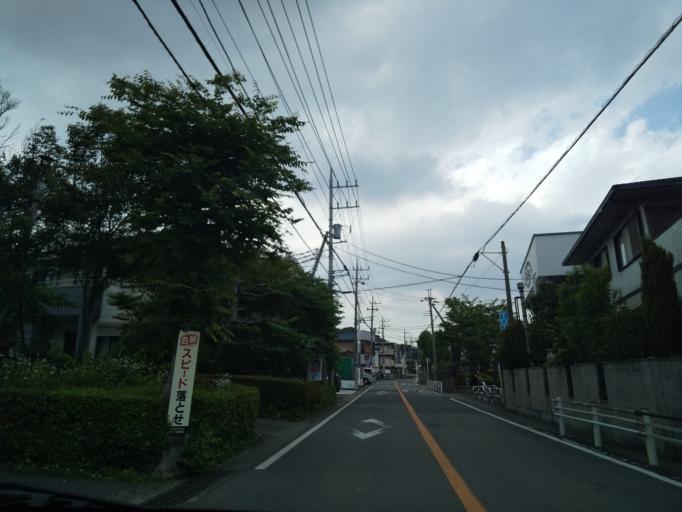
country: JP
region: Tokyo
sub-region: Machida-shi
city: Machida
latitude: 35.5395
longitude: 139.4162
